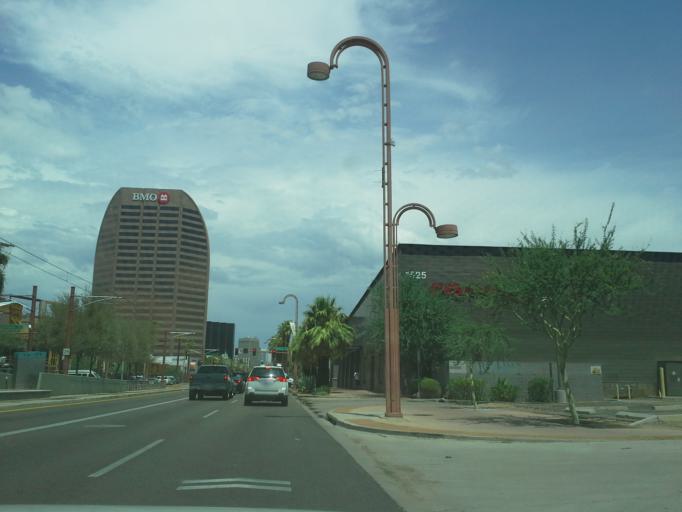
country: US
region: Arizona
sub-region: Maricopa County
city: Phoenix
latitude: 33.4648
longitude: -112.0737
